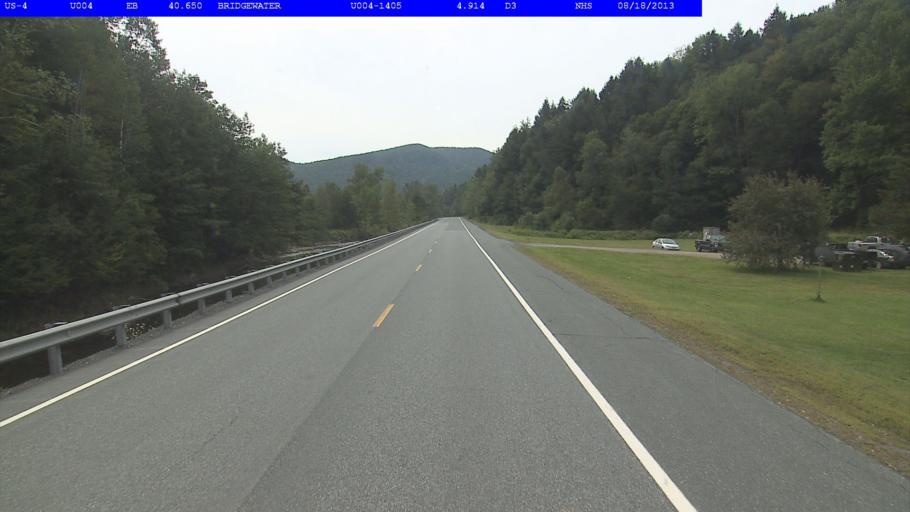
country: US
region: Vermont
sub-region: Windsor County
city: Woodstock
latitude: 43.5950
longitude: -72.6670
